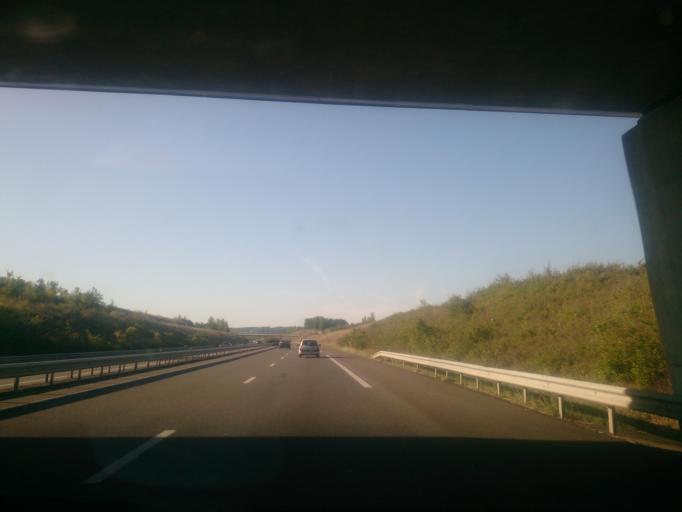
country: FR
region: Midi-Pyrenees
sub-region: Departement du Tarn-et-Garonne
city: Caussade
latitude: 44.2198
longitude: 1.5389
